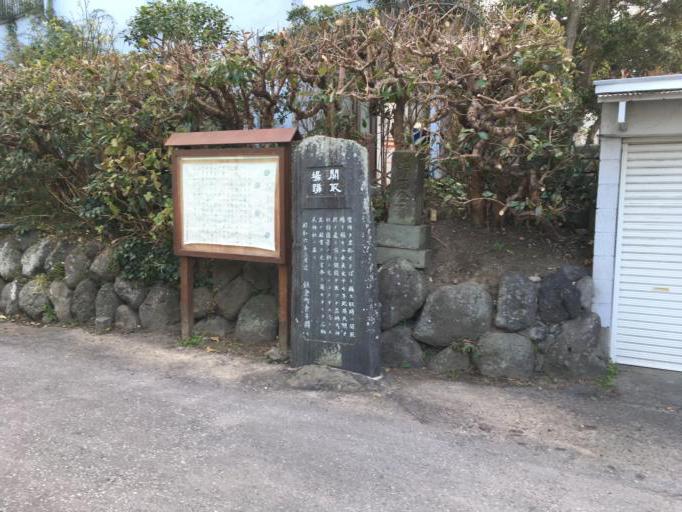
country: JP
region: Kanagawa
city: Kamakura
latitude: 35.3235
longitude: 139.5625
